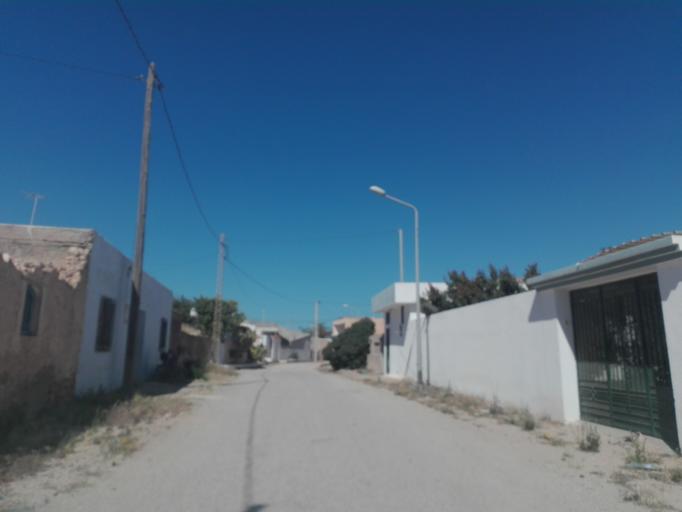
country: TN
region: Safaqis
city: Al Qarmadah
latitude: 34.7131
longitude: 11.1952
